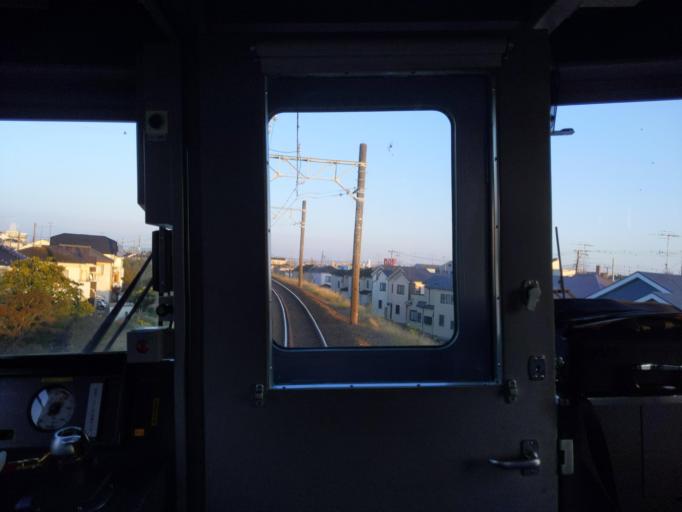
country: JP
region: Saitama
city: Kasukabe
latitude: 35.9739
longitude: 139.7599
